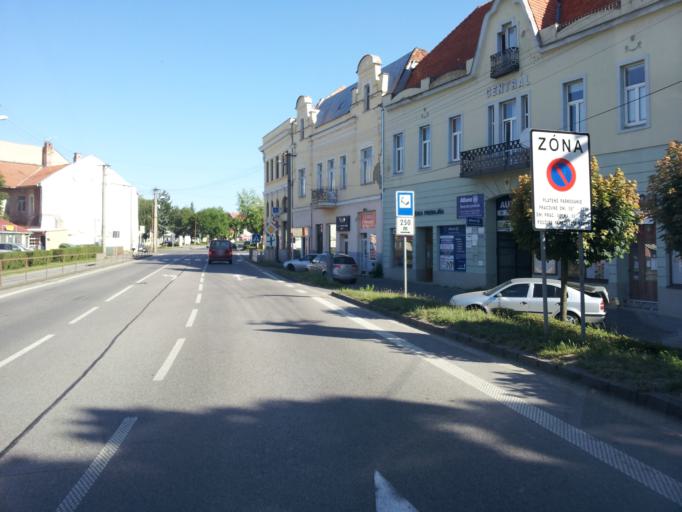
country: SK
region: Nitriansky
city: Sahy
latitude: 48.0686
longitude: 18.9495
